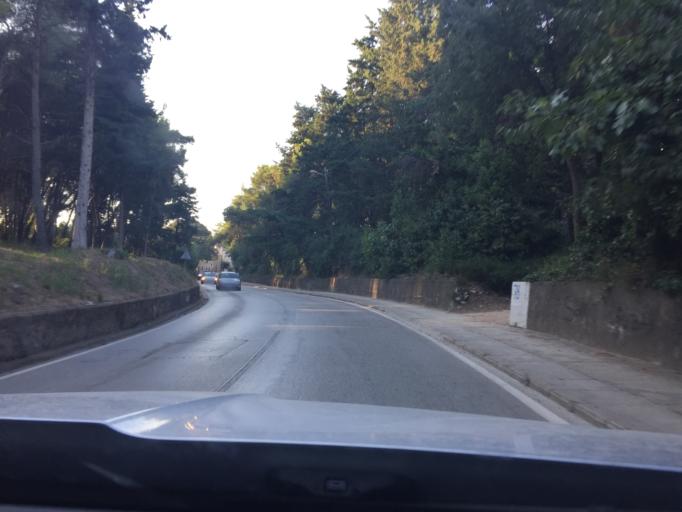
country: HR
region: Zadarska
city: Zadar
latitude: 44.1223
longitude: 15.2332
